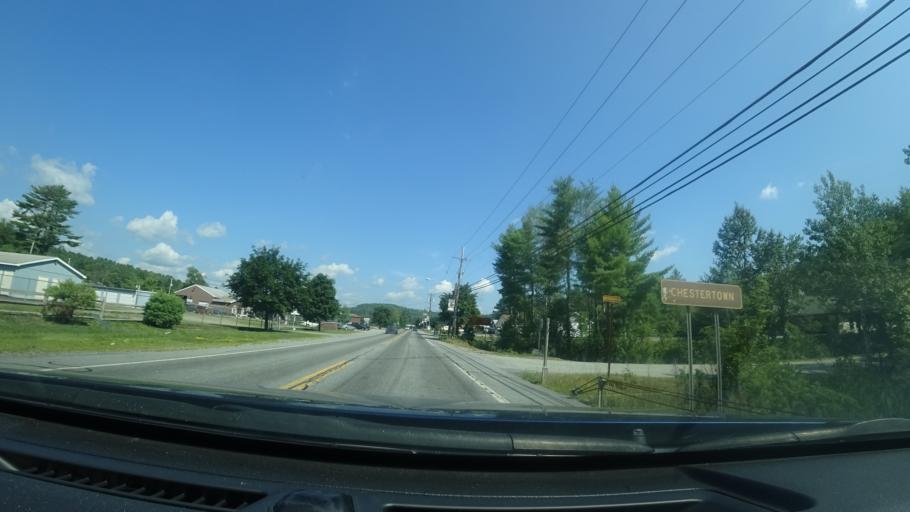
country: US
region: New York
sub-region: Warren County
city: Warrensburg
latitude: 43.6453
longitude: -73.7998
